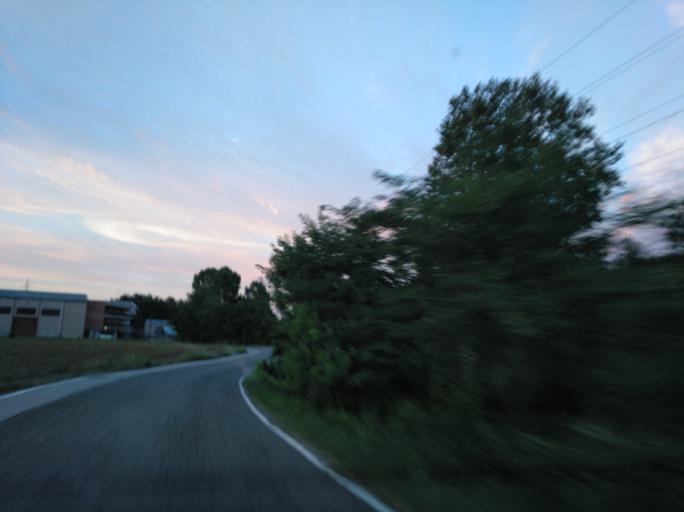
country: ES
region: Catalonia
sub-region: Provincia de Girona
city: Salt
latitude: 41.9565
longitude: 2.7930
